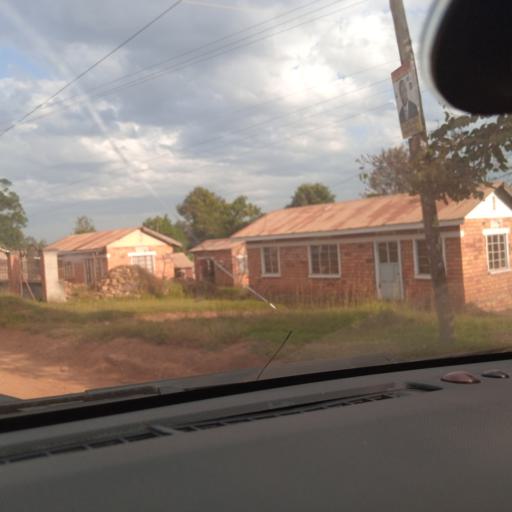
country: UG
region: Central Region
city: Masaka
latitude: -0.3436
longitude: 31.7280
